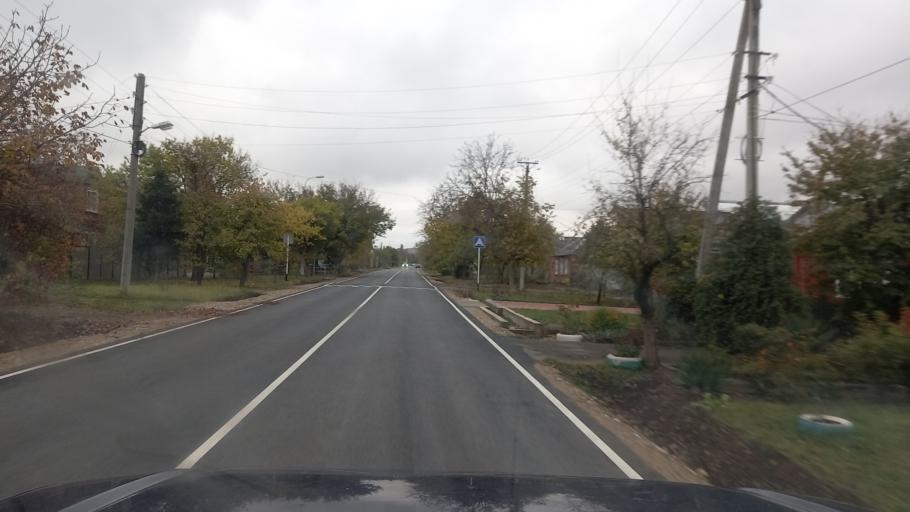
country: RU
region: Adygeya
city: Maykop
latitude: 44.6131
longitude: 40.1223
